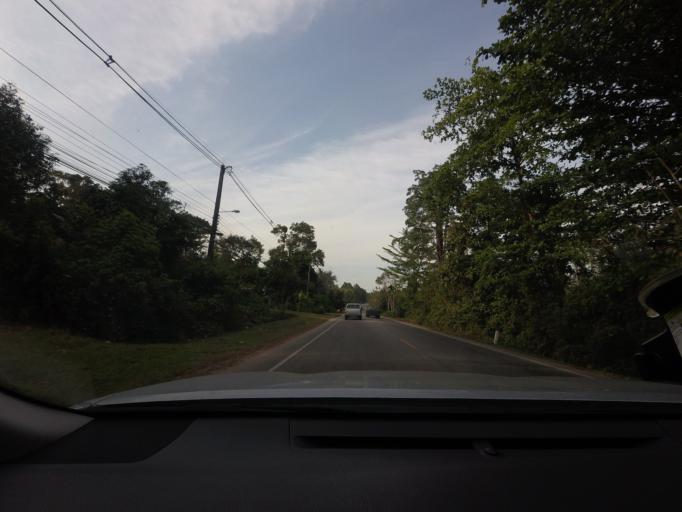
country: TH
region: Narathiwat
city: Ra-ngae
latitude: 6.3081
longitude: 101.7276
